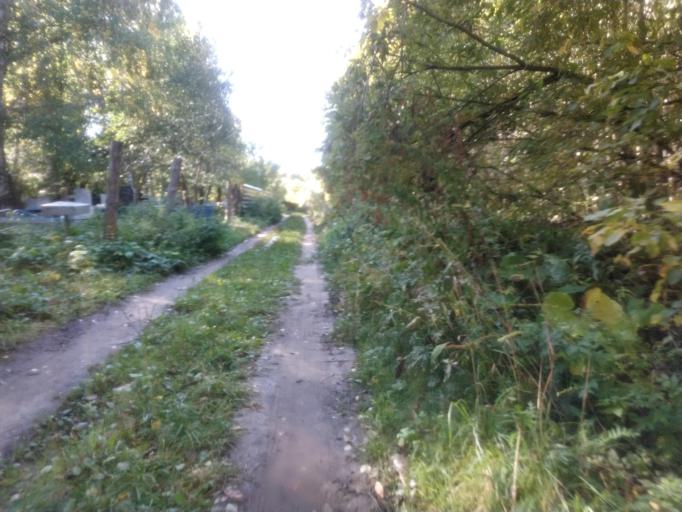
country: RU
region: Chuvashia
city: Novyye Lapsary
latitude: 56.1402
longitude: 47.1403
